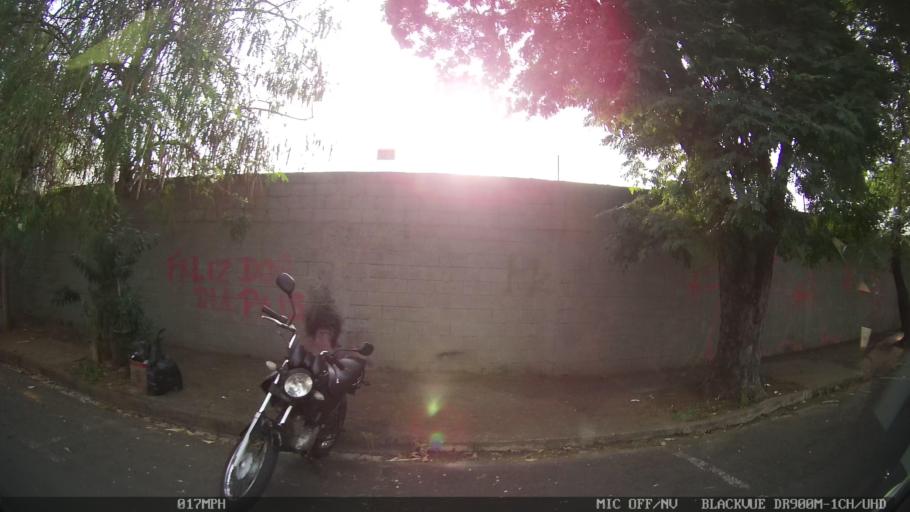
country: BR
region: Sao Paulo
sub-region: Piracicaba
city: Piracicaba
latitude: -22.7300
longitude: -47.6333
